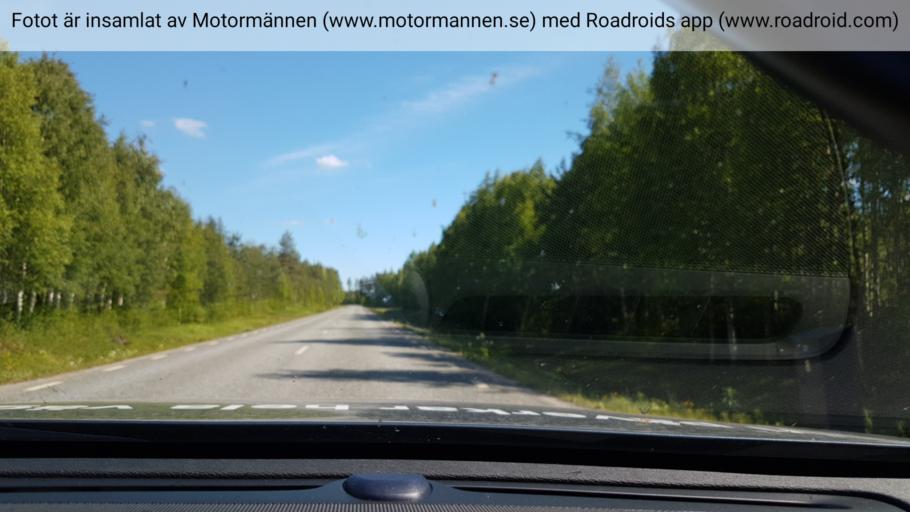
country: SE
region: Vaesterbotten
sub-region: Lycksele Kommun
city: Lycksele
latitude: 64.6102
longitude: 18.4952
